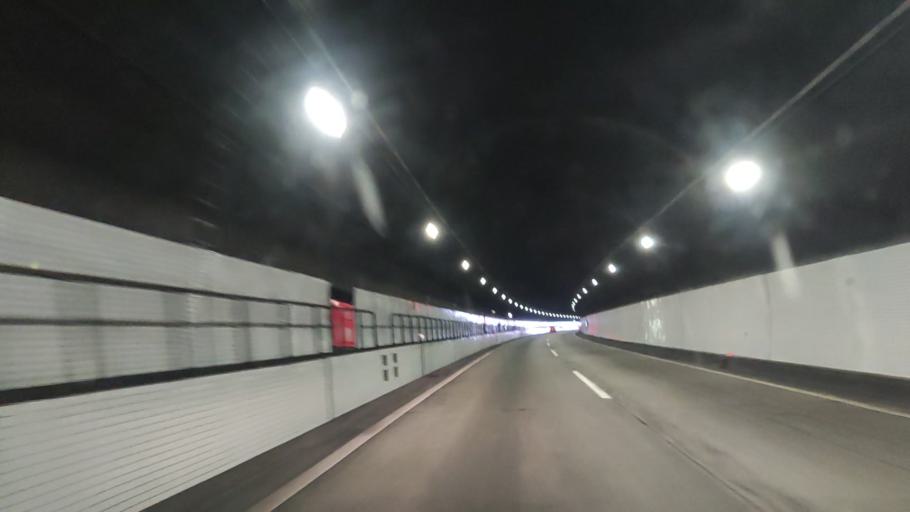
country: JP
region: Ehime
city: Niihama
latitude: 33.9165
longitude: 133.3019
